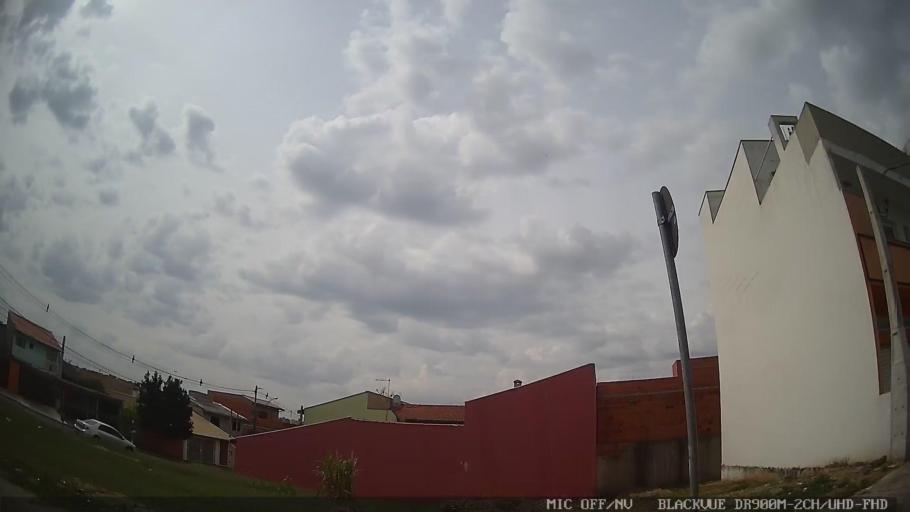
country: BR
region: Sao Paulo
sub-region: Indaiatuba
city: Indaiatuba
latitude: -23.1303
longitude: -47.2506
